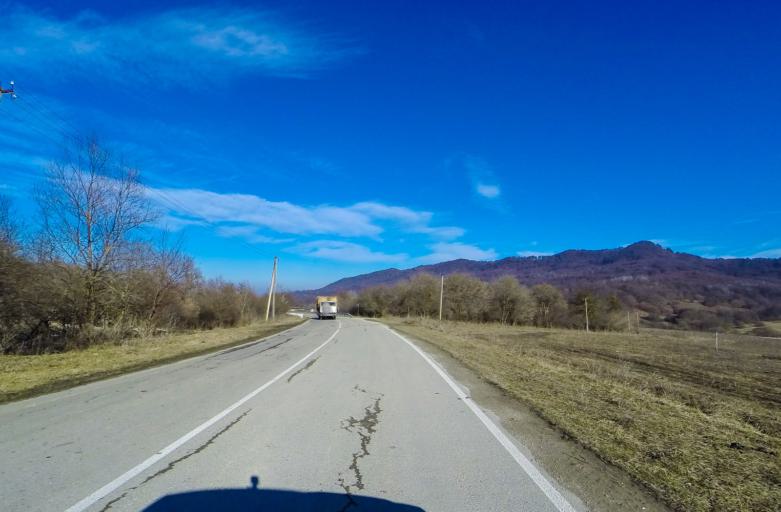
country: RU
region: Kabardino-Balkariya
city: Belaya Rechka
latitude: 43.4003
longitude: 43.5909
